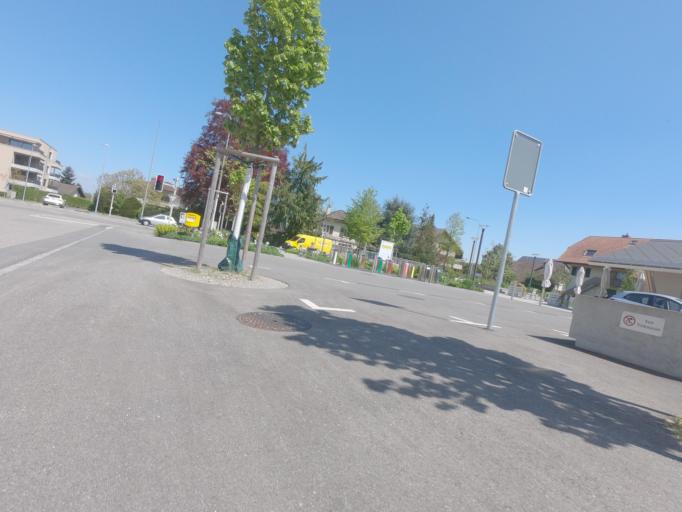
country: CH
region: Bern
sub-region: Biel/Bienne District
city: Brugg
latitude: 47.1213
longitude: 7.2883
